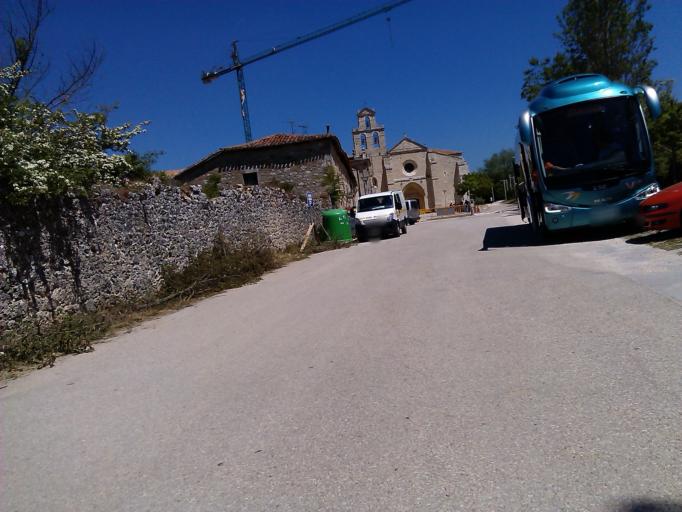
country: ES
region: Castille and Leon
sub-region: Provincia de Burgos
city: Barrios de Colina
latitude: 42.3761
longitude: -3.4384
